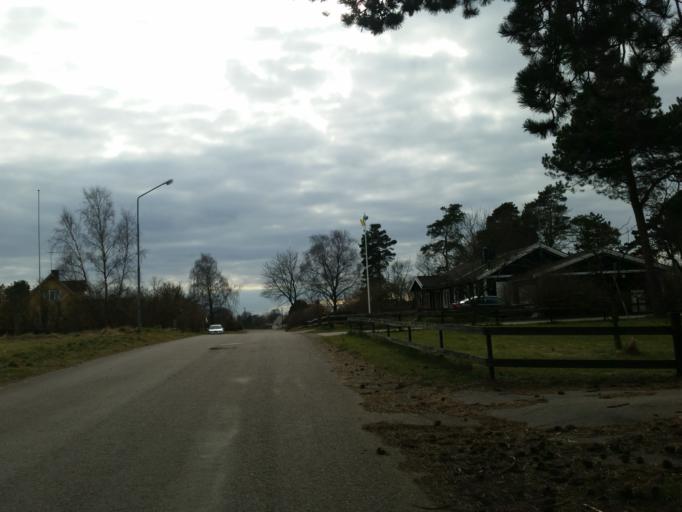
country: SE
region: Kalmar
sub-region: Morbylanga Kommun
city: Sodra Sandby
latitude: 56.6055
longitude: 16.6467
